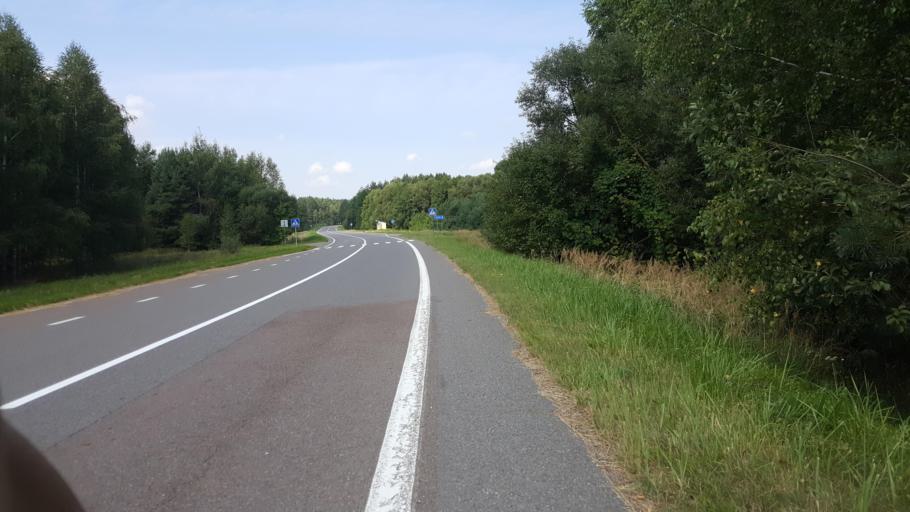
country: BY
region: Brest
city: Kamyanyuki
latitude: 52.5582
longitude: 23.6308
